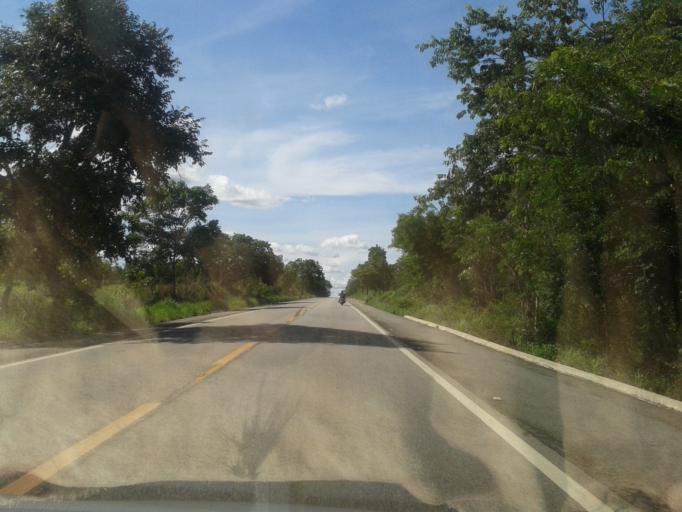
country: BR
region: Goias
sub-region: Mozarlandia
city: Mozarlandia
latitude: -15.2819
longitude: -50.4750
